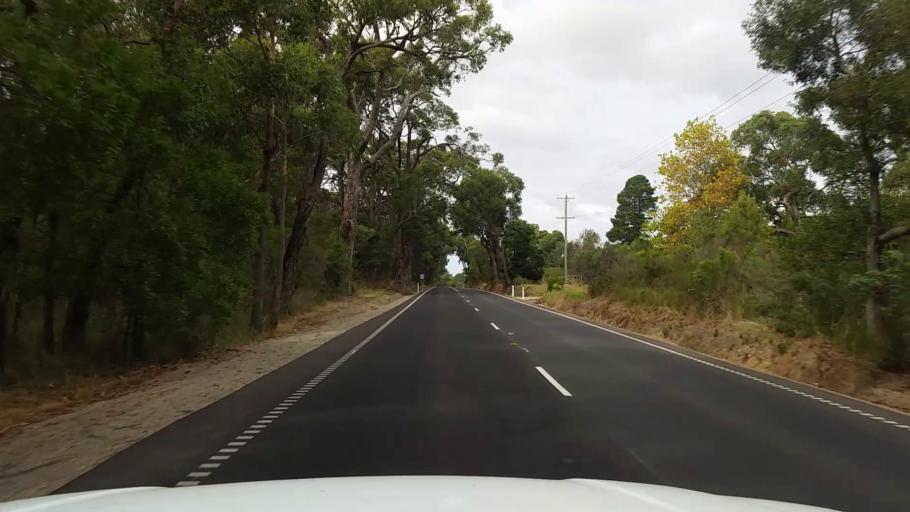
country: AU
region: Victoria
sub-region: Mornington Peninsula
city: Balnarring
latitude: -38.3416
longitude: 145.0991
